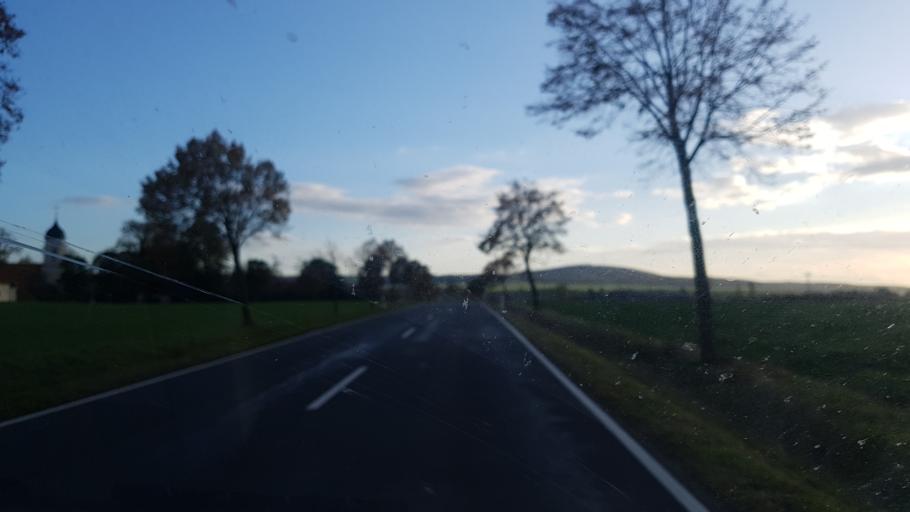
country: DE
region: Saxony
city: Dahlen
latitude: 51.3411
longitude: 13.0296
